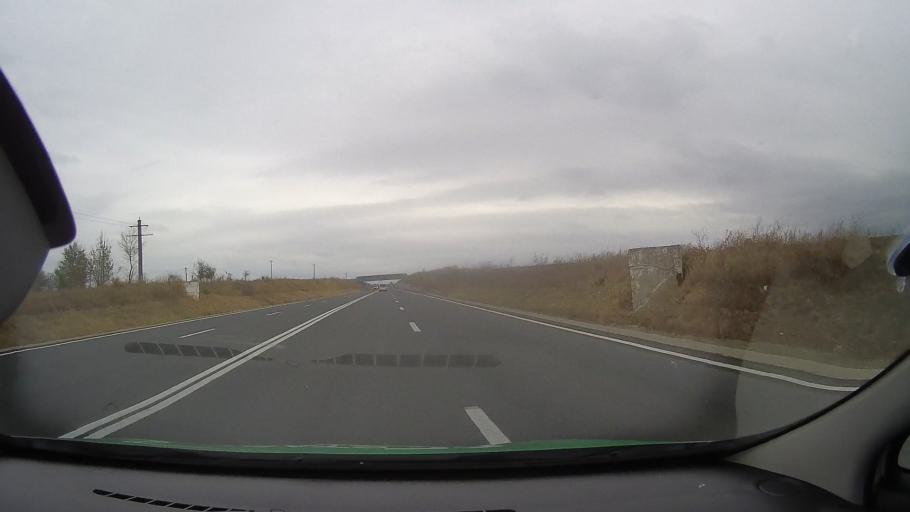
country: RO
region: Constanta
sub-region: Comuna Nicolae Balcescu
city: Nicolae Balcescu
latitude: 44.3820
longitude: 28.4029
